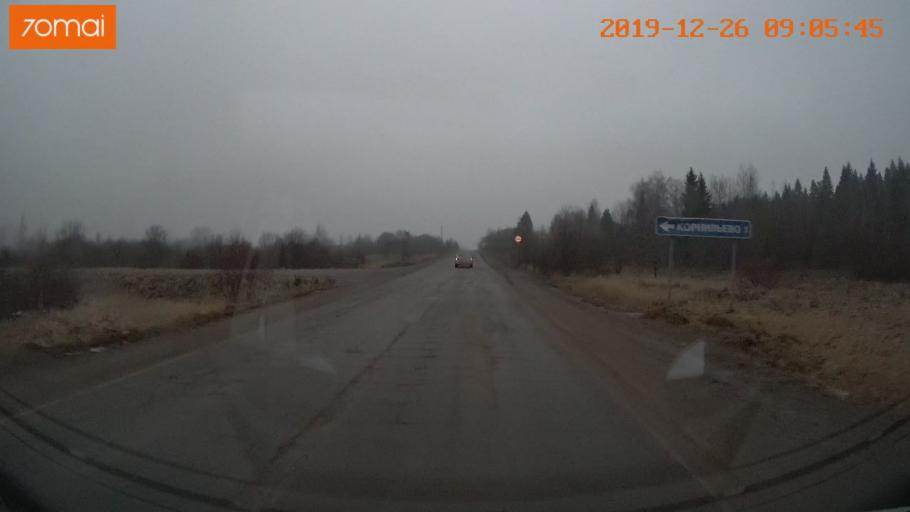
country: RU
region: Vologda
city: Gryazovets
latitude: 58.8288
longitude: 40.2565
